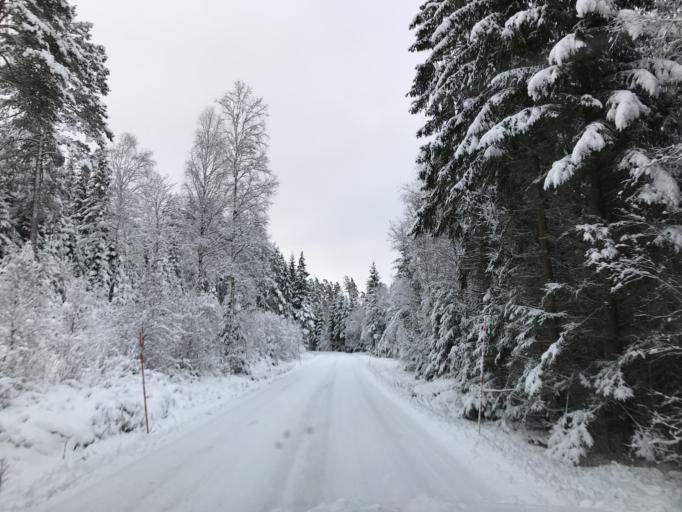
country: SE
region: Vaestra Goetaland
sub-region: Boras Kommun
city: Sandared
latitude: 57.8067
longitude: 12.6963
